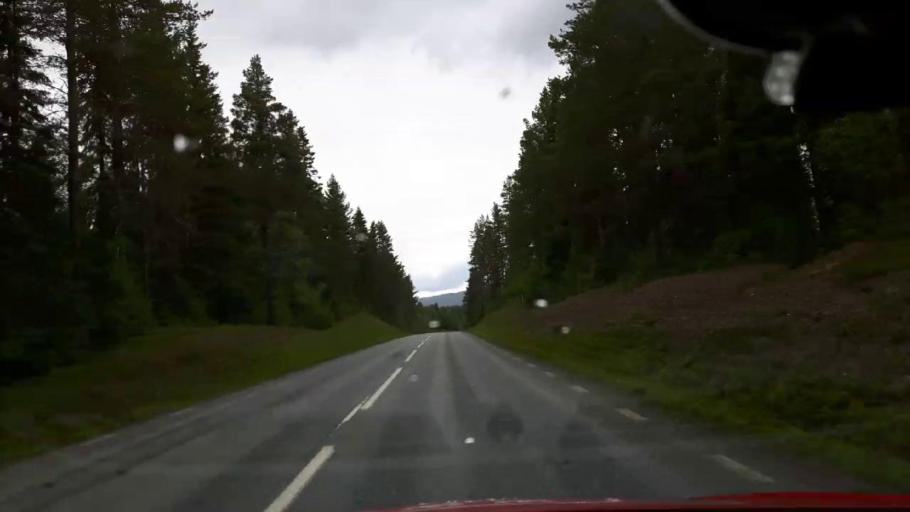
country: SE
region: Jaemtland
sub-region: Krokoms Kommun
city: Krokom
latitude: 63.4218
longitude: 14.2216
